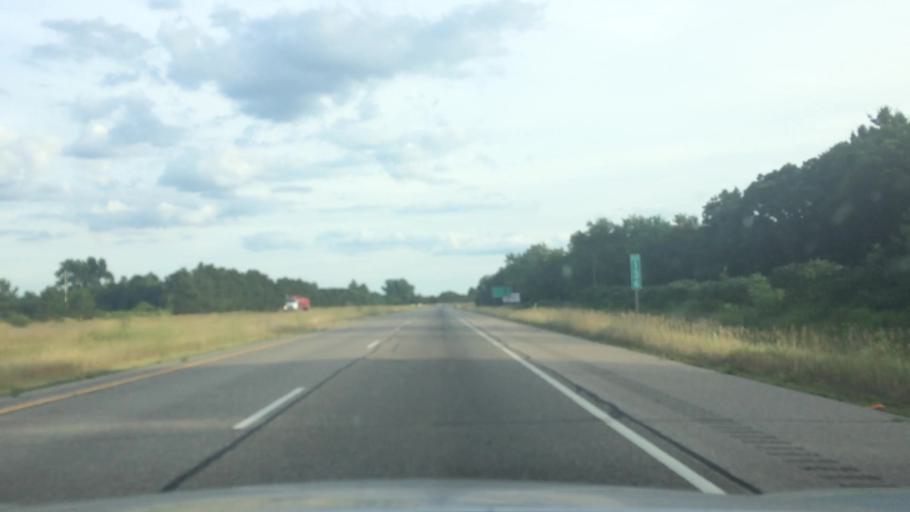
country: US
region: Wisconsin
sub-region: Portage County
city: Plover
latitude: 44.2028
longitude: -89.5234
